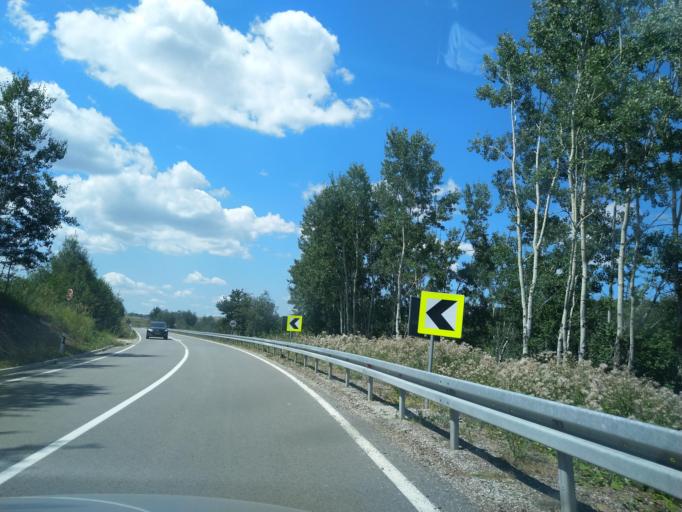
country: RS
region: Central Serbia
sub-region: Zlatiborski Okrug
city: Sjenica
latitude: 43.3283
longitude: 19.8828
